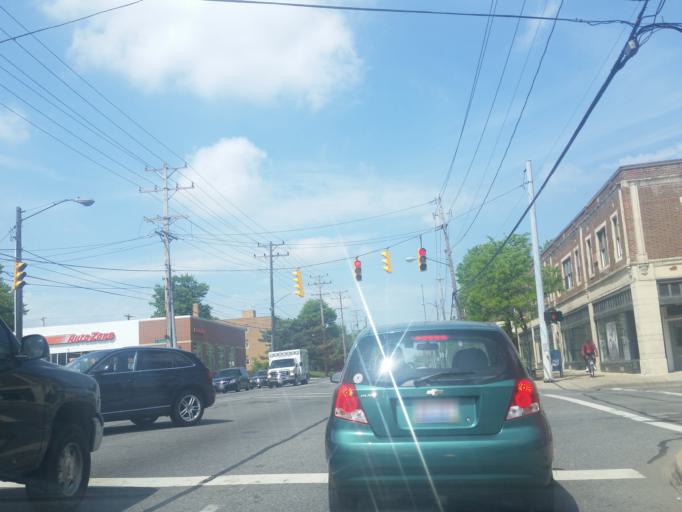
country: US
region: Ohio
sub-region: Cuyahoga County
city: Cleveland Heights
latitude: 41.5208
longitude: -81.5387
